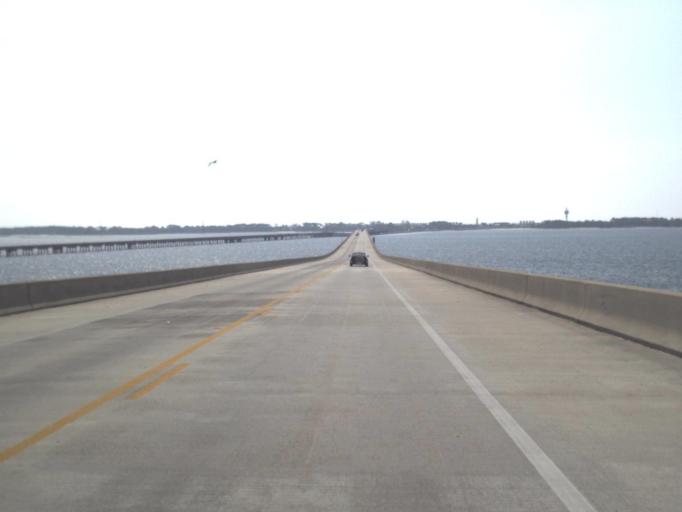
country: US
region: Florida
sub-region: Franklin County
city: Eastpoint
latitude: 29.6807
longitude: -84.8772
